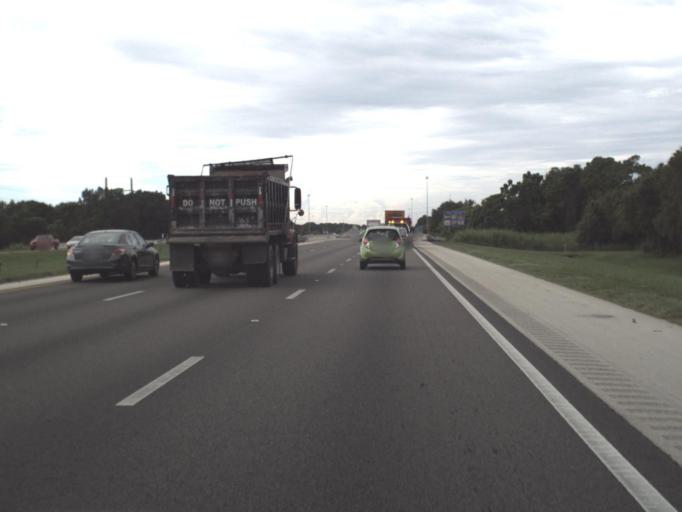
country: US
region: Florida
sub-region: Sarasota County
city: Lake Sarasota
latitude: 27.3103
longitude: -82.4483
